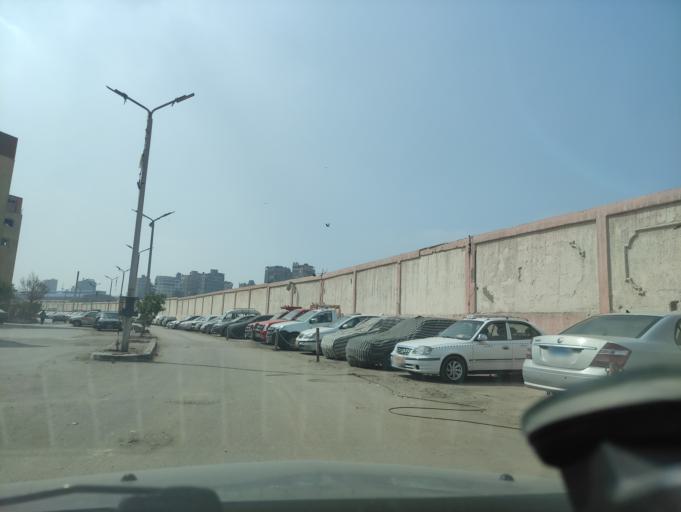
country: EG
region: Muhafazat al Qahirah
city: Cairo
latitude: 30.0783
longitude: 31.2575
